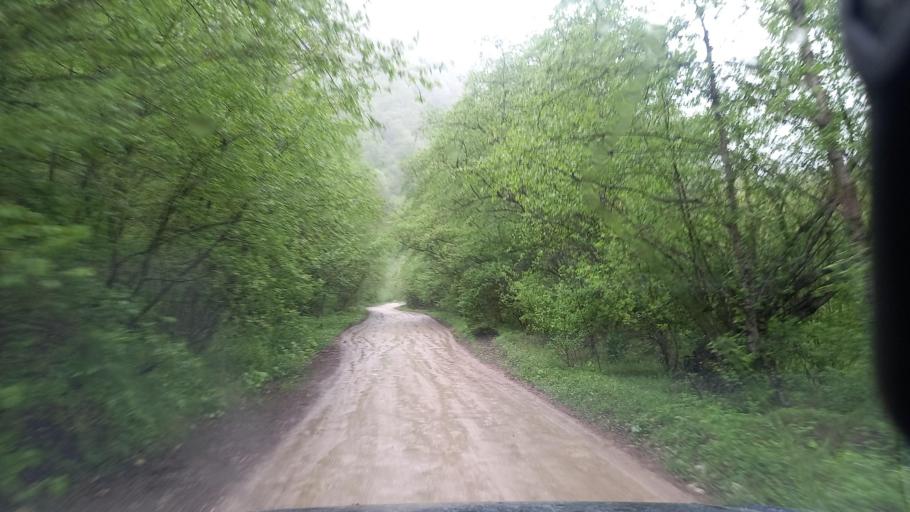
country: RU
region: Kabardino-Balkariya
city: Gundelen
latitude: 43.5816
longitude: 43.1134
